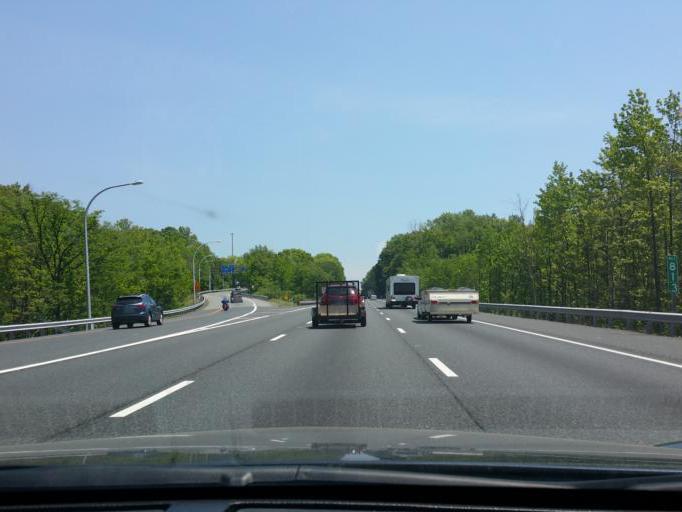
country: US
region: Maryland
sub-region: Harford County
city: Riverside
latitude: 39.4935
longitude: -76.2361
